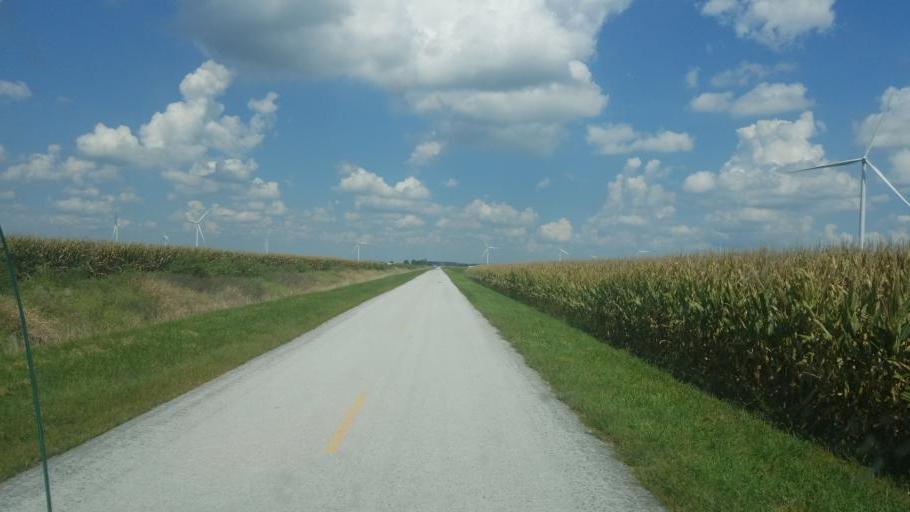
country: US
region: Ohio
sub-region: Hardin County
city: Ada
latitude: 40.7671
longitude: -83.7287
